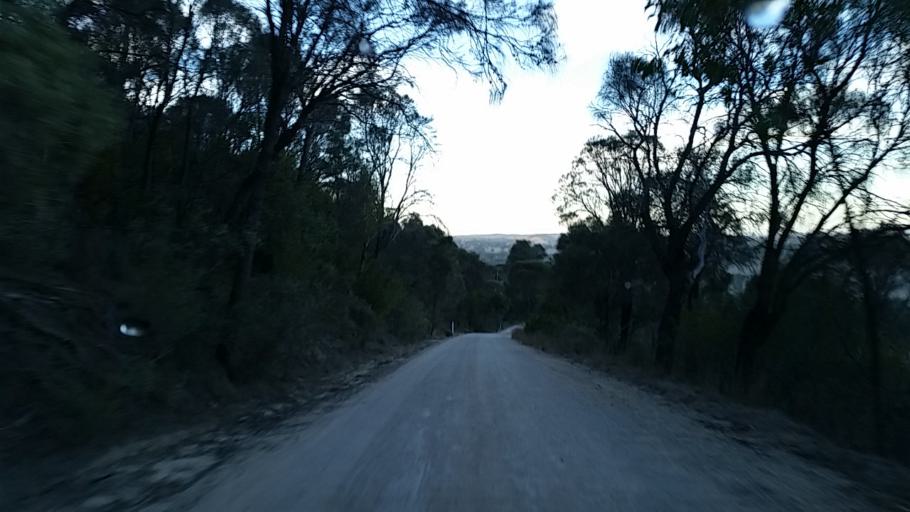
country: AU
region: South Australia
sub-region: Mount Barker
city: Nairne
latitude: -35.0655
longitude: 138.9234
